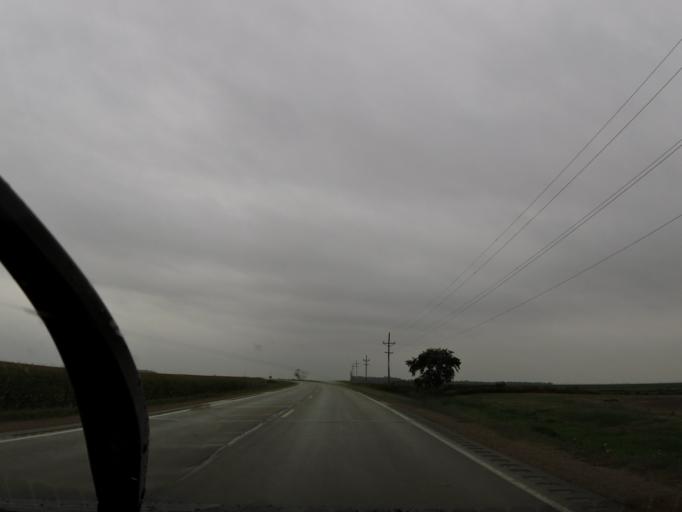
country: US
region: Minnesota
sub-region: Marshall County
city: Warren
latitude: 48.4350
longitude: -96.8676
